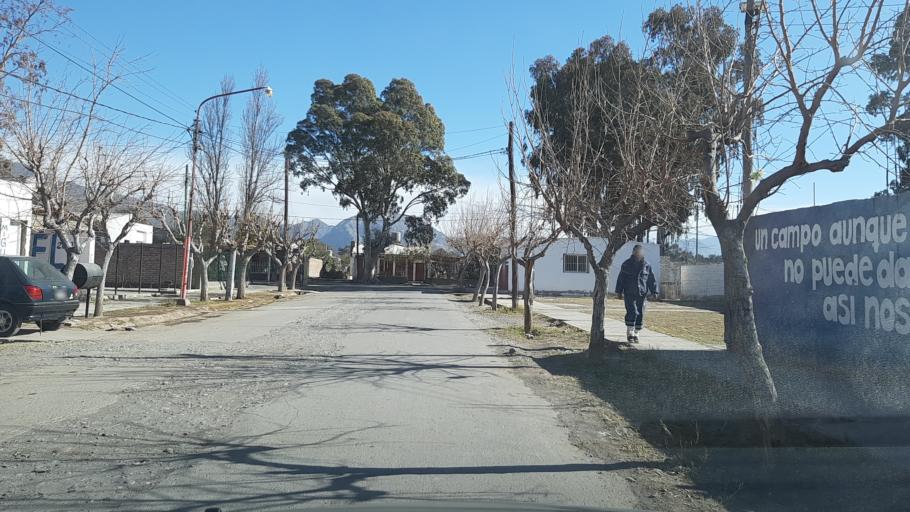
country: AR
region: San Juan
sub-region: Departamento de Zonda
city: Zonda
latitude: -31.5478
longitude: -68.7285
